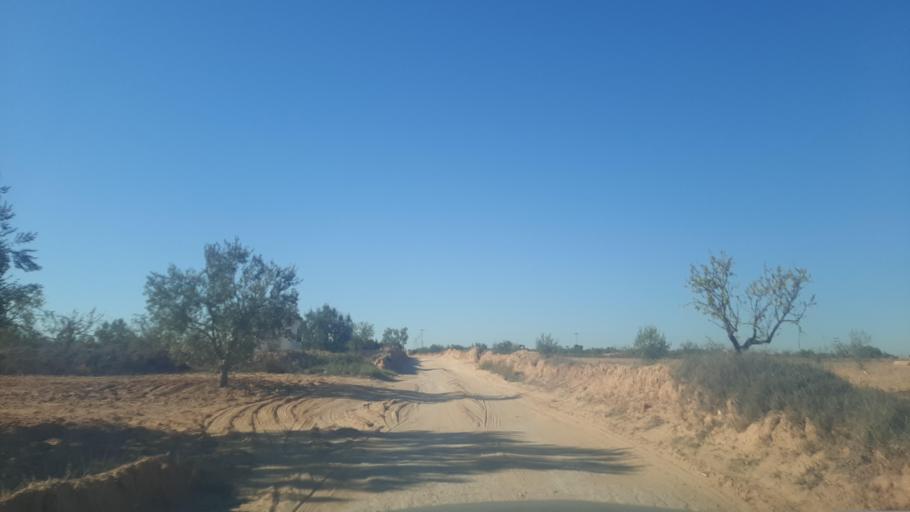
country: TN
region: Safaqis
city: Sfax
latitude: 34.8939
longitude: 10.5954
